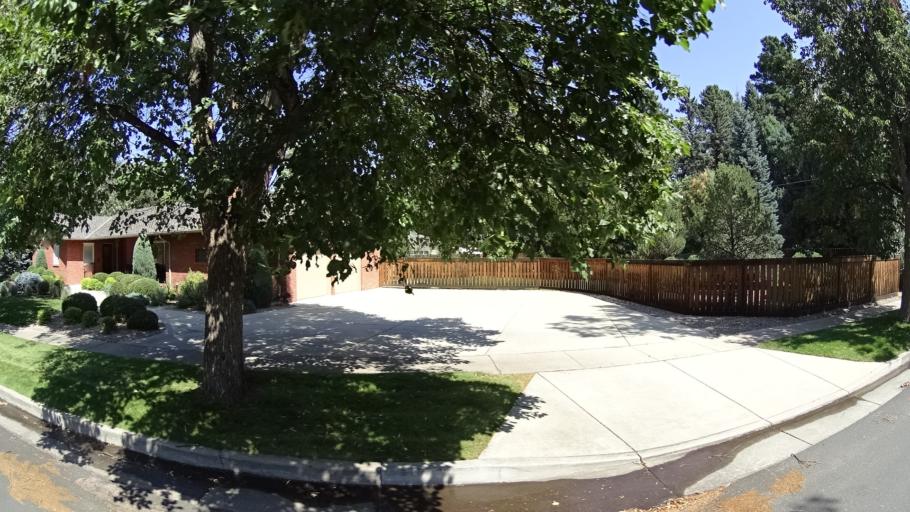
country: US
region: Colorado
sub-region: El Paso County
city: Colorado Springs
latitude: 38.8566
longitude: -104.8284
